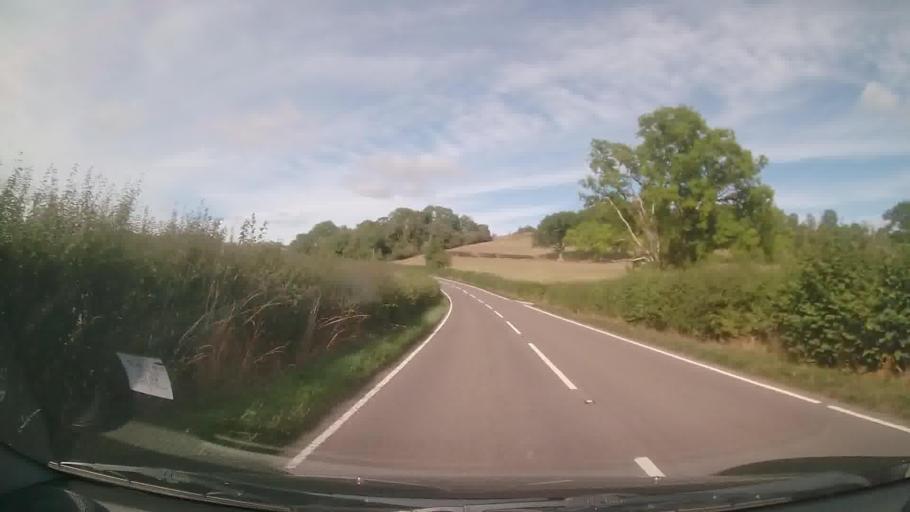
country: GB
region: England
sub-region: Shropshire
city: Lydham
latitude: 52.5277
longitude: -2.9890
